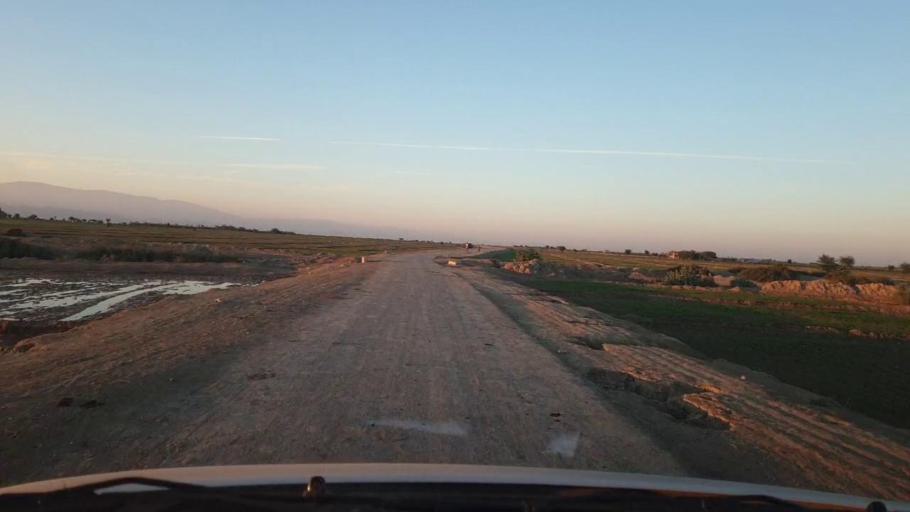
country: PK
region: Sindh
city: Johi
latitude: 26.8325
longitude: 67.4424
